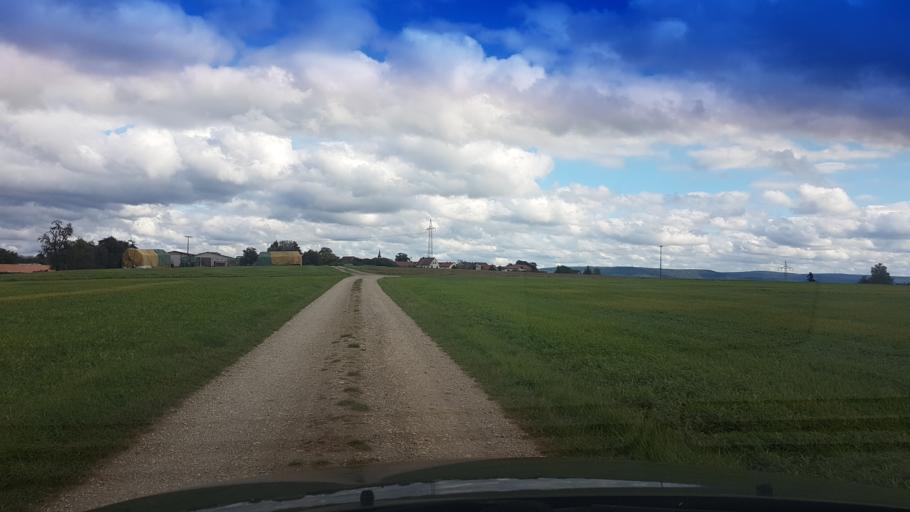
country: DE
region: Bavaria
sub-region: Upper Franconia
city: Zapfendorf
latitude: 49.9805
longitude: 10.9331
